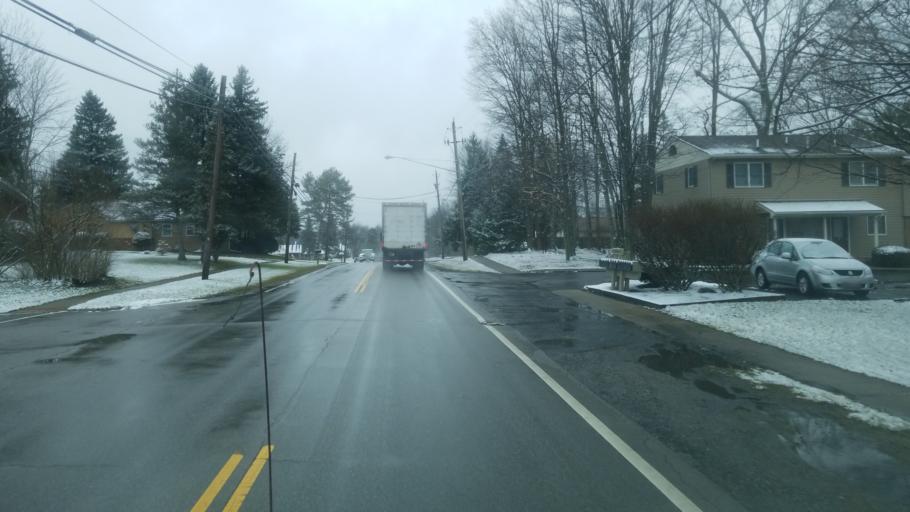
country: US
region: Ohio
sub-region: Portage County
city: Garrettsville
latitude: 41.2747
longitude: -81.0985
